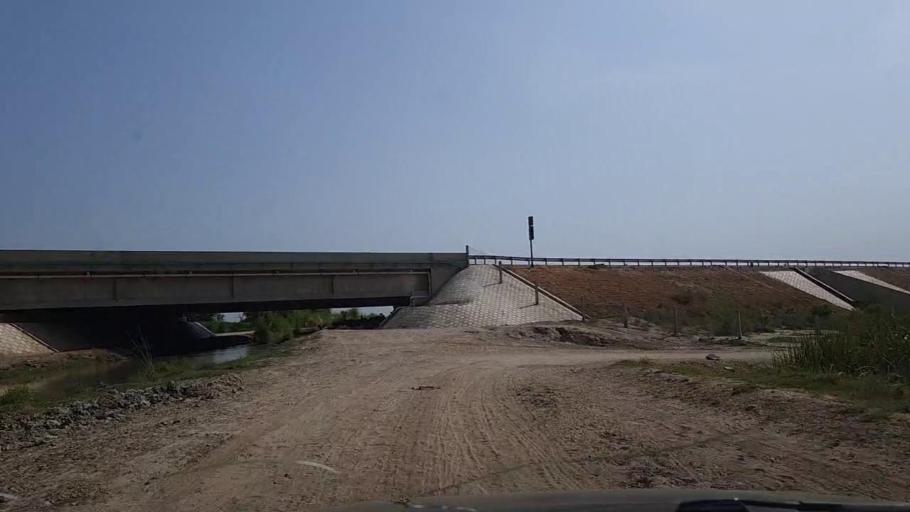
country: PK
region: Sindh
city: Ghotki
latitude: 28.0633
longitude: 69.3823
